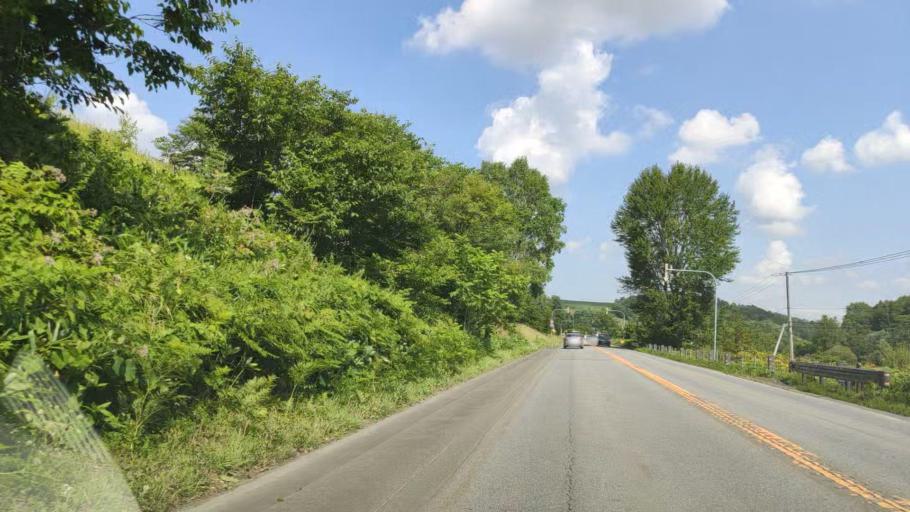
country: JP
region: Hokkaido
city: Shimo-furano
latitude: 43.5623
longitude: 142.4350
